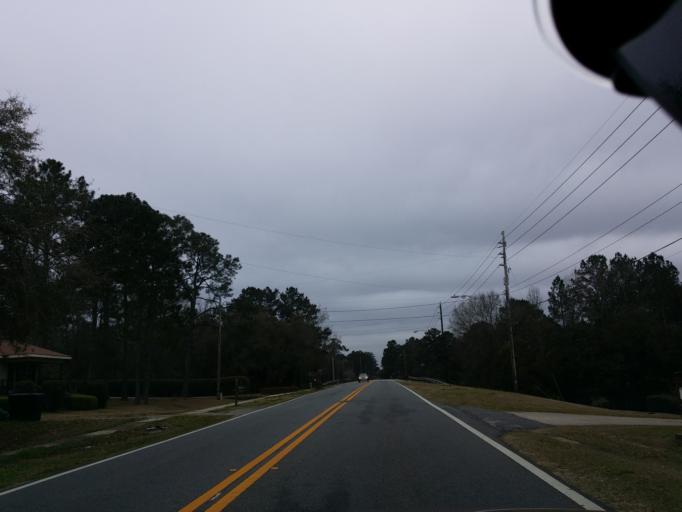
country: US
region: Florida
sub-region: Leon County
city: Tallahassee
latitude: 30.5026
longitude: -84.2300
